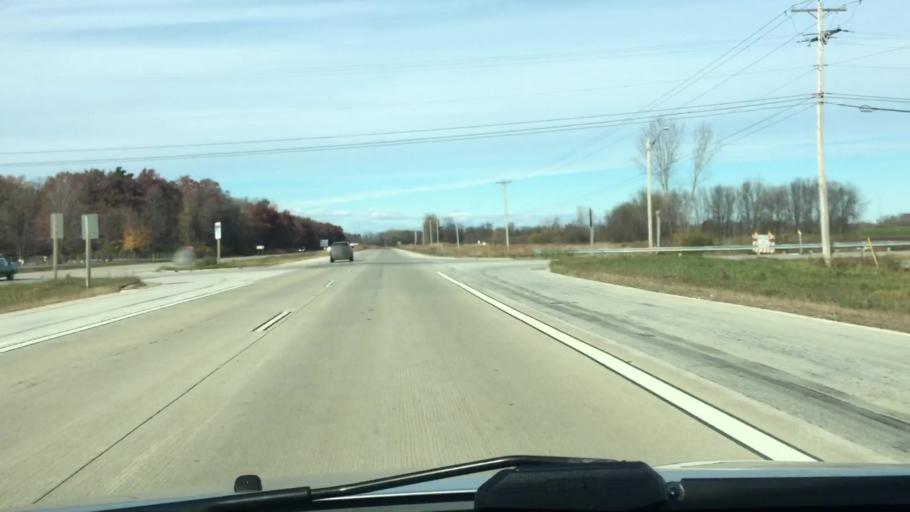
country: US
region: Wisconsin
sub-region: Brown County
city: Bellevue
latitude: 44.5525
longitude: -87.8811
